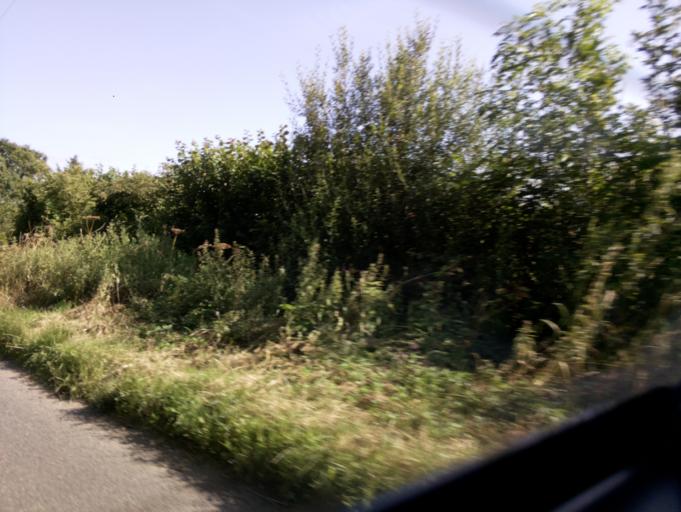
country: GB
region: England
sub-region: Oxfordshire
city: Bampton
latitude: 51.7158
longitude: -1.5274
